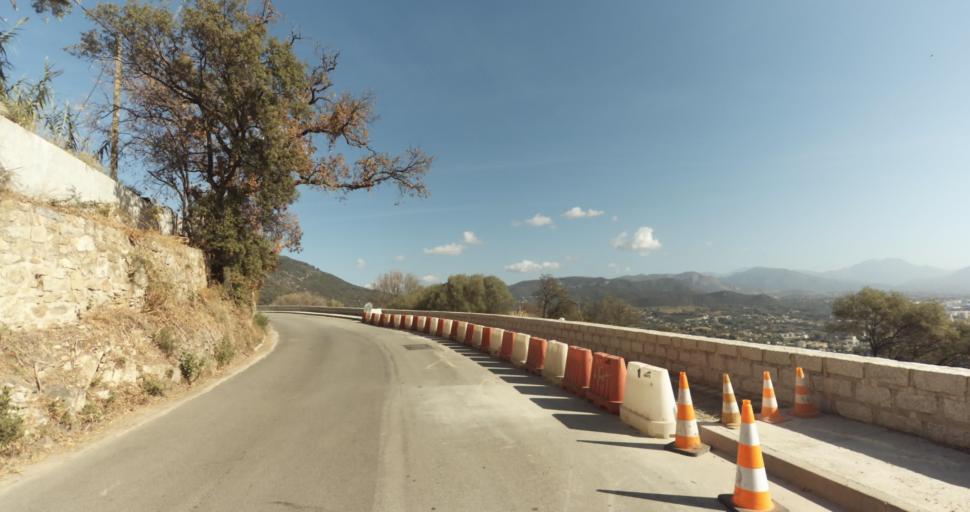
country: FR
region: Corsica
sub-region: Departement de la Corse-du-Sud
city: Ajaccio
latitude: 41.9255
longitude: 8.7182
